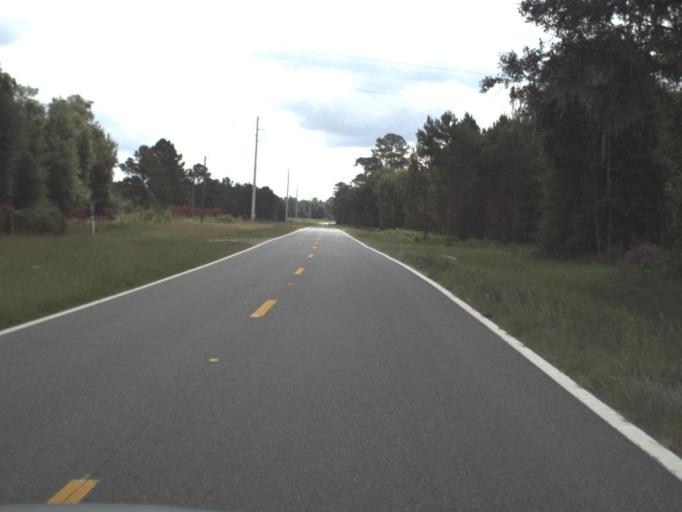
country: US
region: Florida
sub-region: Union County
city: Lake Butler
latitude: 29.9133
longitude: -82.3897
